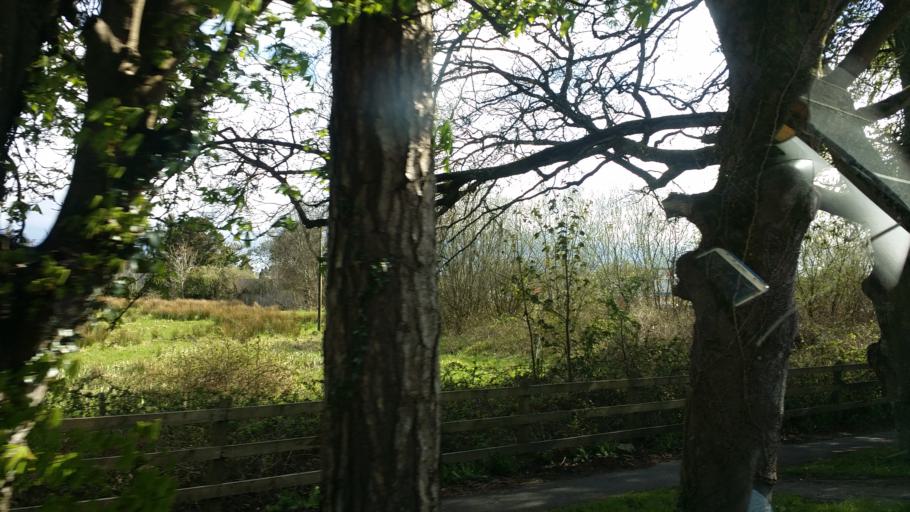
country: IE
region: Ulster
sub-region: County Donegal
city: Ballyshannon
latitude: 54.4778
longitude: -8.0954
